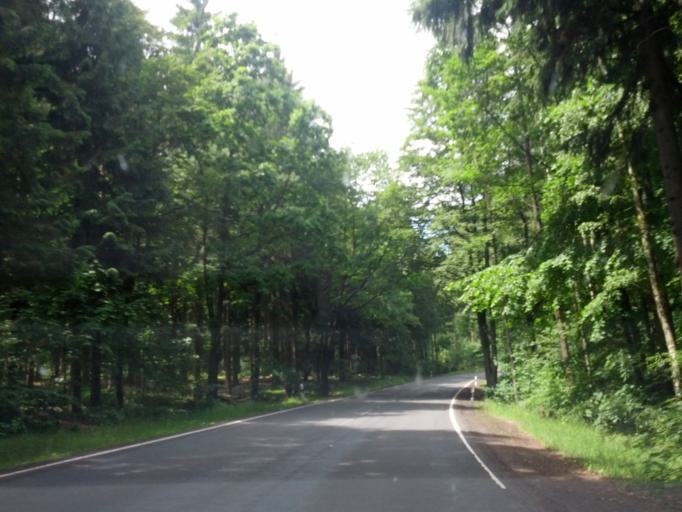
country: DE
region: Thuringia
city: Friedrichroda
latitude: 50.8628
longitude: 10.5521
